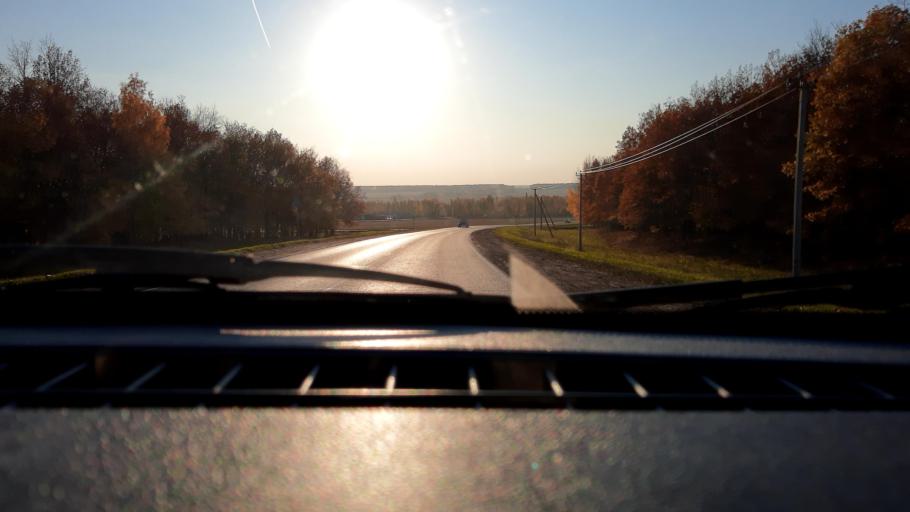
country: RU
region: Bashkortostan
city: Avdon
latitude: 54.8203
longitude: 55.7124
